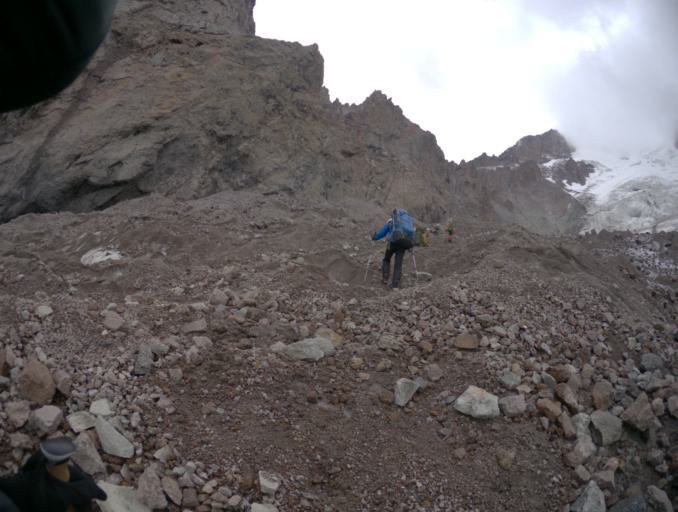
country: RU
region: Kabardino-Balkariya
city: Terskol
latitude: 43.3794
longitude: 42.3979
